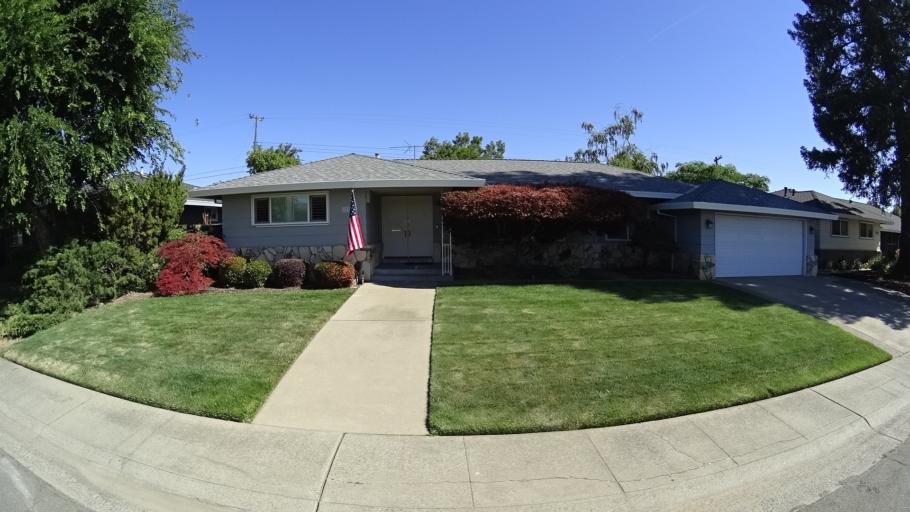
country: US
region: California
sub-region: Sacramento County
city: Parkway
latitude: 38.5007
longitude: -121.5145
